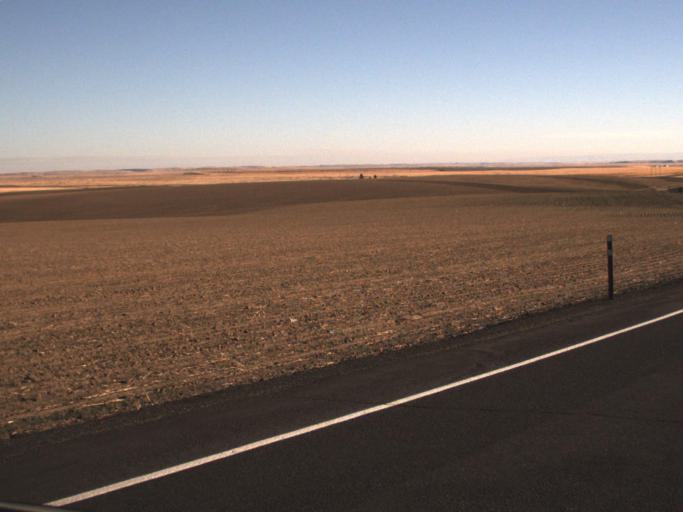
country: US
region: Washington
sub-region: Adams County
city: Ritzville
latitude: 47.0097
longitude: -118.3521
